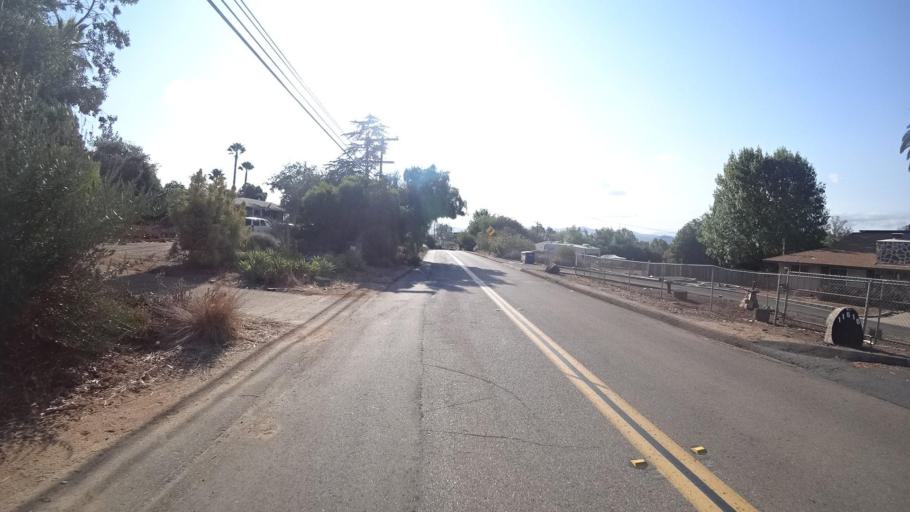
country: US
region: California
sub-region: San Diego County
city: Eucalyptus Hills
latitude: 32.8887
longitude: -116.9429
